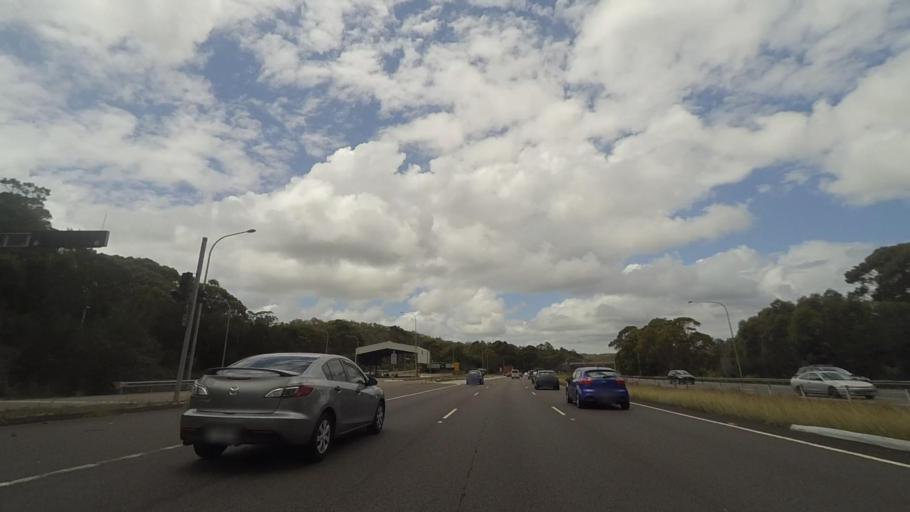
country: AU
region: New South Wales
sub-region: Gosford Shire
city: Point Clare
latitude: -33.4546
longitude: 151.2062
